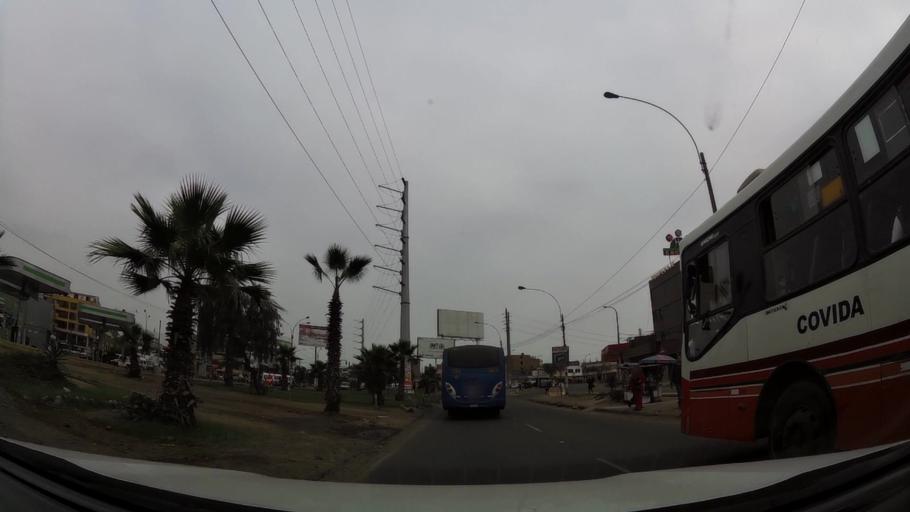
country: PE
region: Lima
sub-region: Lima
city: Independencia
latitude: -11.9952
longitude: -77.0843
